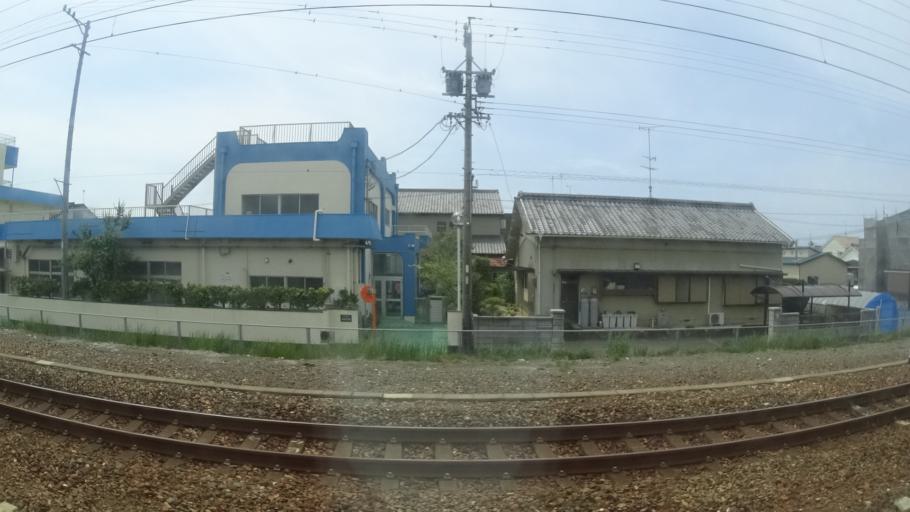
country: JP
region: Shizuoka
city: Kosai-shi
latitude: 34.6857
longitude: 137.6222
